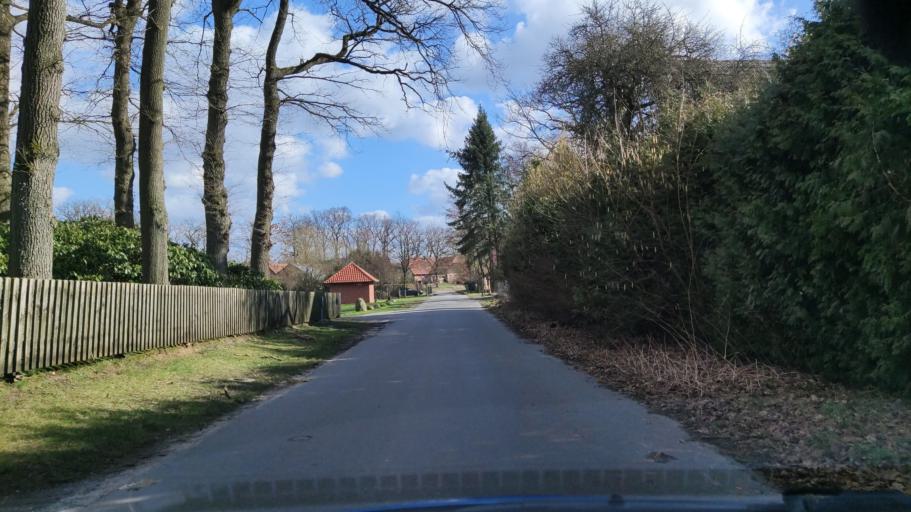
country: DE
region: Lower Saxony
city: Eldingen
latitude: 52.7033
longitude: 10.3426
